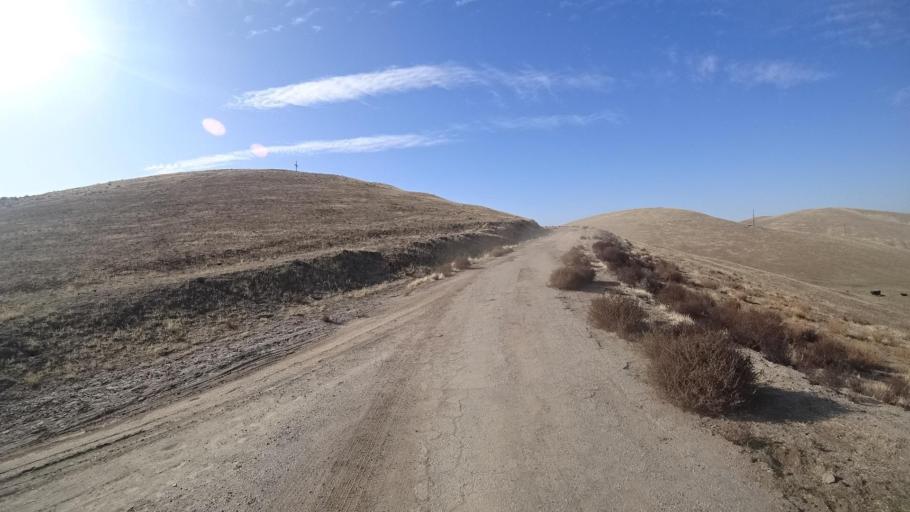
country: US
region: California
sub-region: Kern County
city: Oildale
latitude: 35.4960
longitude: -118.8595
